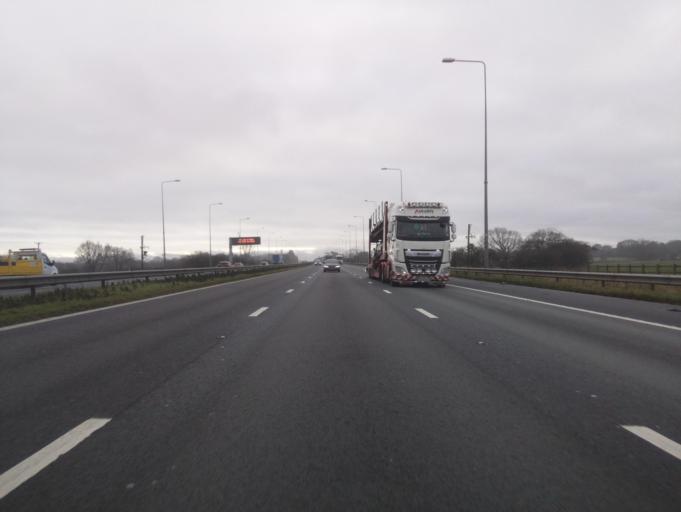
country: GB
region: England
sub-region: Borough of Wigan
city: Shevington
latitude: 53.6039
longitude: -2.6907
